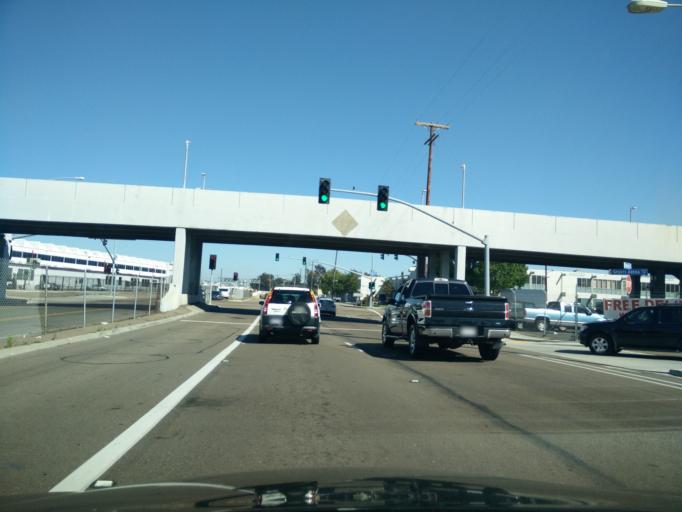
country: US
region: California
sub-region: San Diego County
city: San Diego
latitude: 32.7475
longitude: -117.1983
